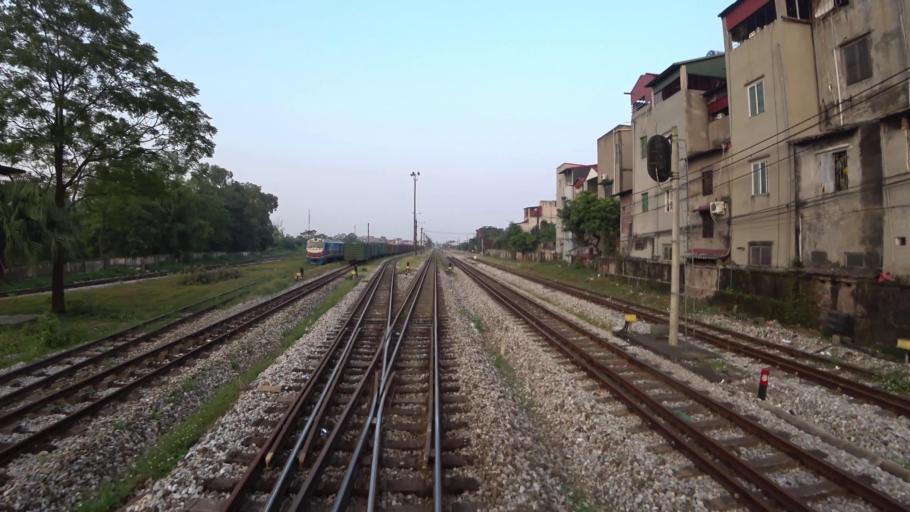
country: VN
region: Ha Noi
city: Dong Anh
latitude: 21.0963
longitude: 105.9106
